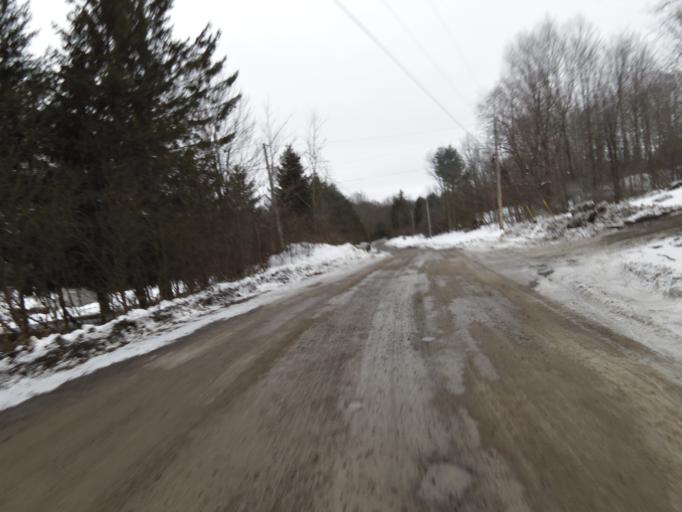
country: CA
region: Ontario
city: Carleton Place
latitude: 45.1704
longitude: -76.2320
